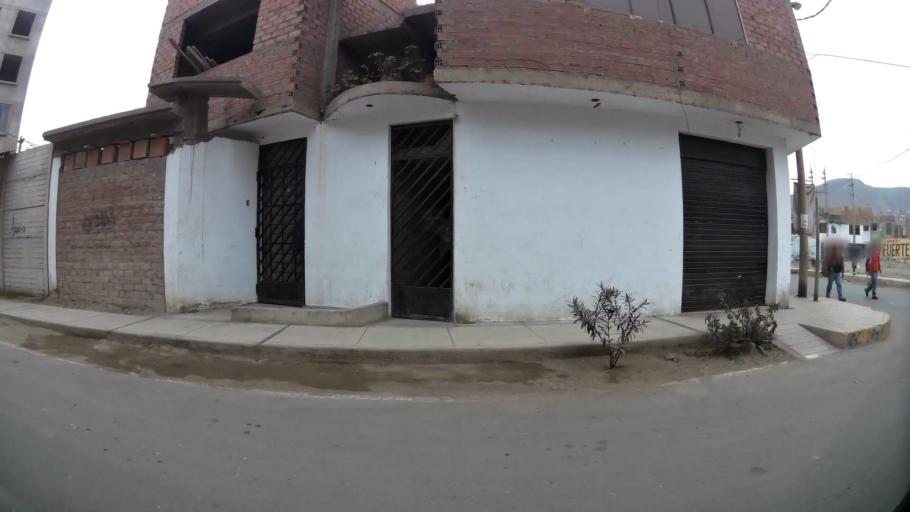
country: PE
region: Lima
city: Ventanilla
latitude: -11.9360
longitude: -77.0885
